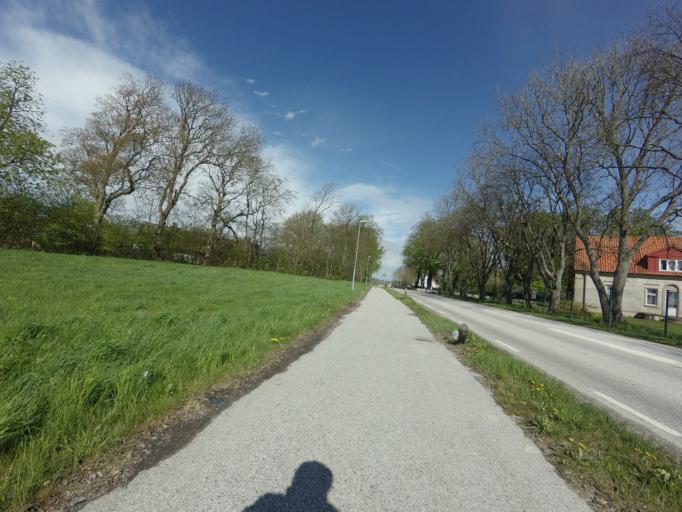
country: SE
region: Skane
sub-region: Malmo
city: Tygelsjo
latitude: 55.5011
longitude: 12.9963
